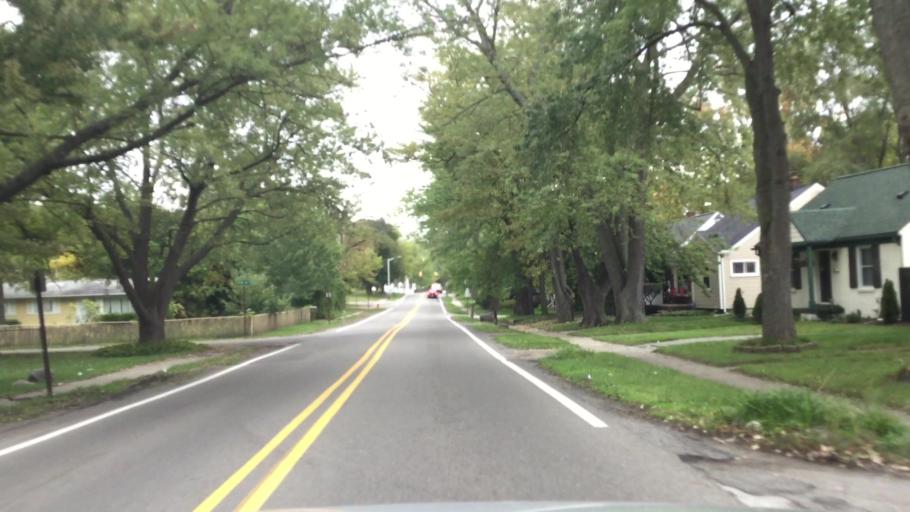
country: US
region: Michigan
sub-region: Oakland County
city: Sylvan Lake
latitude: 42.6299
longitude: -83.3288
